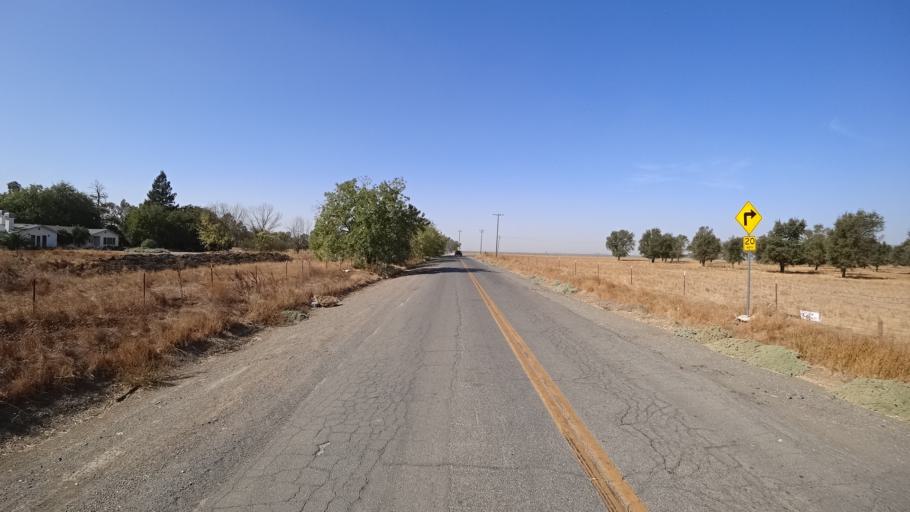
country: US
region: California
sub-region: Yolo County
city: Davis
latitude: 38.4876
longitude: -121.6939
